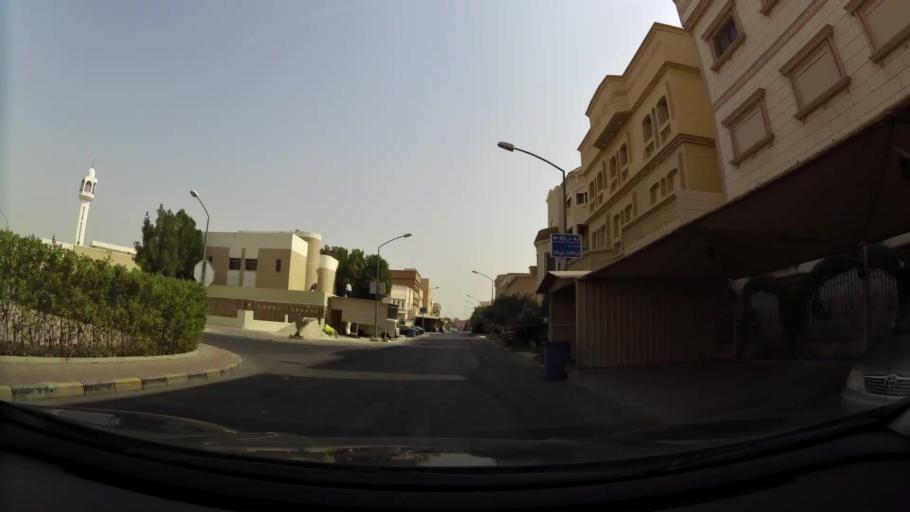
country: KW
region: Muhafazat al Jahra'
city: Al Jahra'
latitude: 29.3032
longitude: 47.7154
